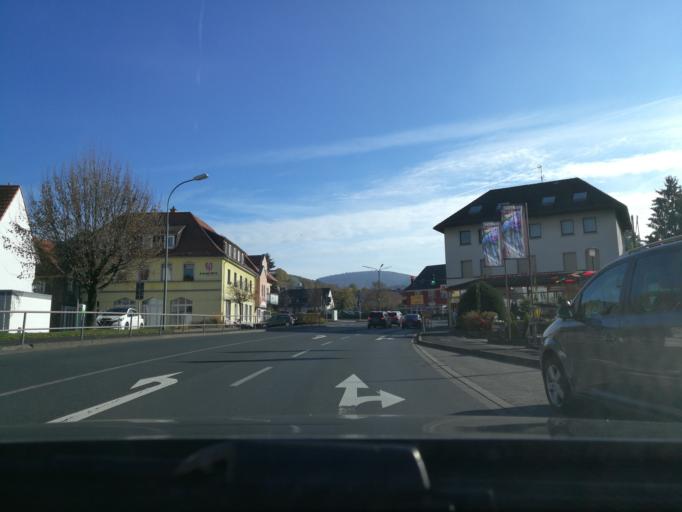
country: DE
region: Hesse
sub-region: Regierungsbezirk Kassel
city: Gersfeld
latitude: 50.4501
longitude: 9.9189
